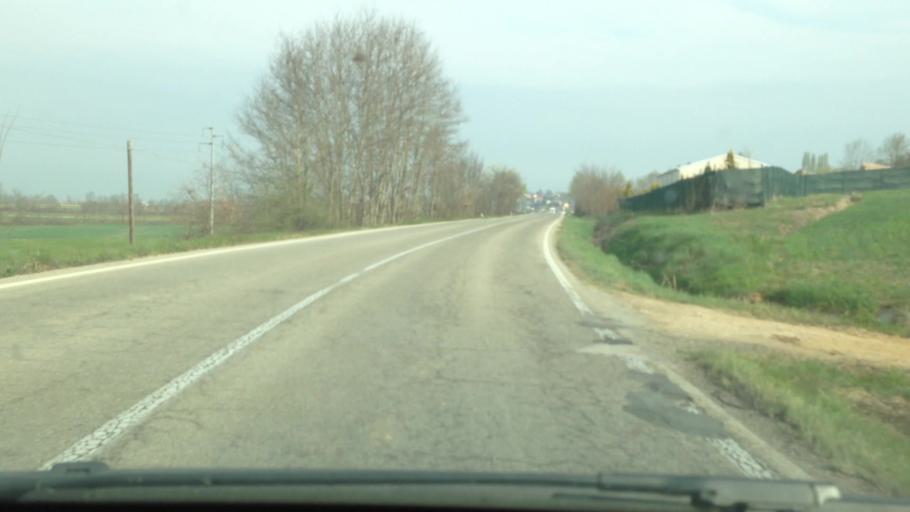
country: IT
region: Piedmont
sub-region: Provincia di Torino
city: Pralormo
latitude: 44.8430
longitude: 7.9108
